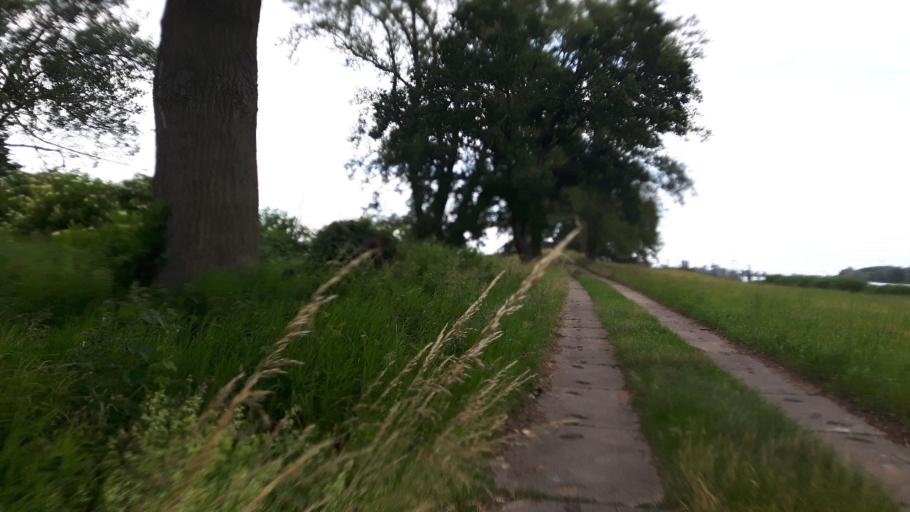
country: PL
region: West Pomeranian Voivodeship
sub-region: Powiat gryfinski
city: Widuchowa
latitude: 53.1278
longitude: 14.3794
